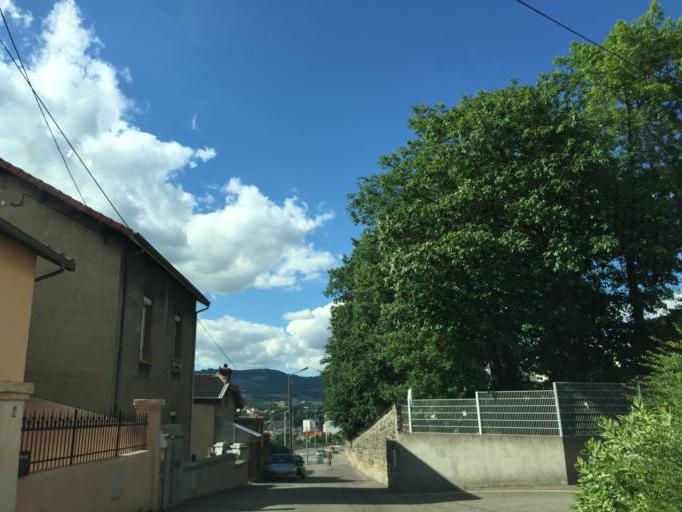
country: FR
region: Rhone-Alpes
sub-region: Departement de la Loire
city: Saint-Chamond
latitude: 45.4672
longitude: 4.5112
